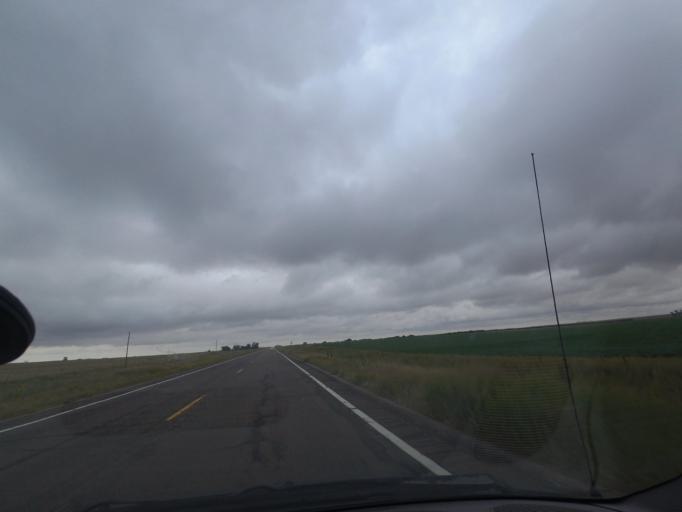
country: US
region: Colorado
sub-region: Yuma County
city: Yuma
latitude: 39.6699
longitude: -102.8957
